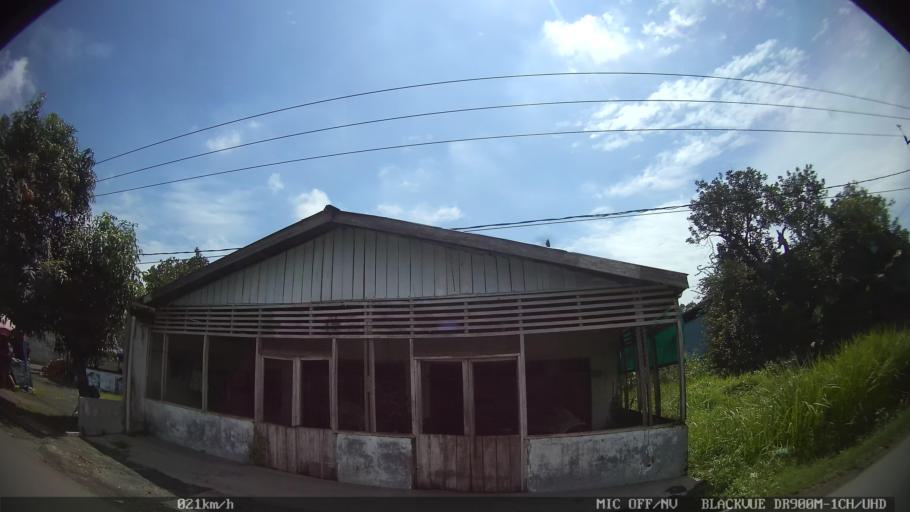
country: ID
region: North Sumatra
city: Medan
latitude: 3.5999
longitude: 98.7472
